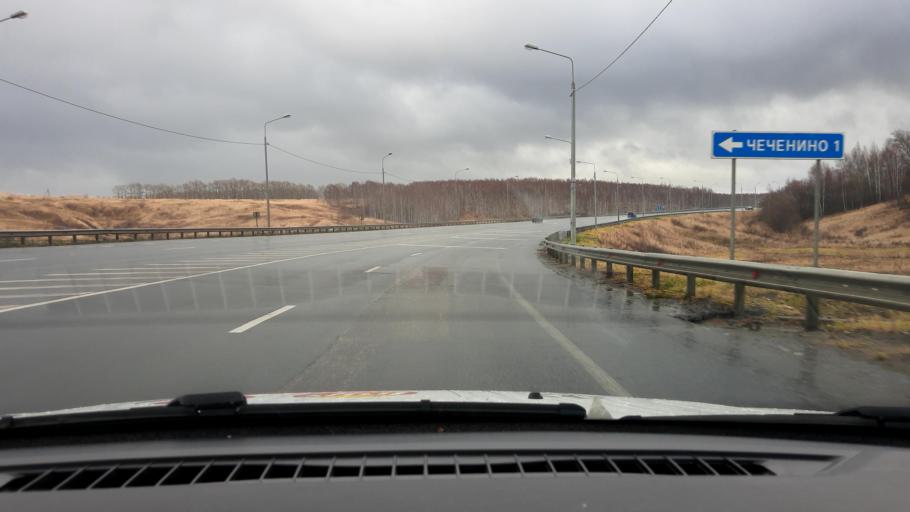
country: RU
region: Nizjnij Novgorod
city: Pamyat' Parizhskoy Kommuny
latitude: 56.0273
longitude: 44.6212
